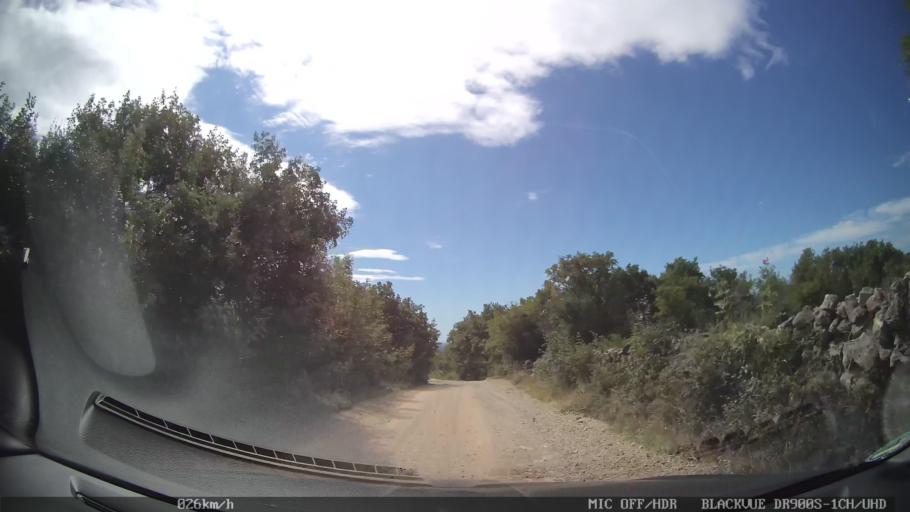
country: HR
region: Primorsko-Goranska
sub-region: Grad Krk
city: Krk
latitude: 45.0379
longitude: 14.5338
